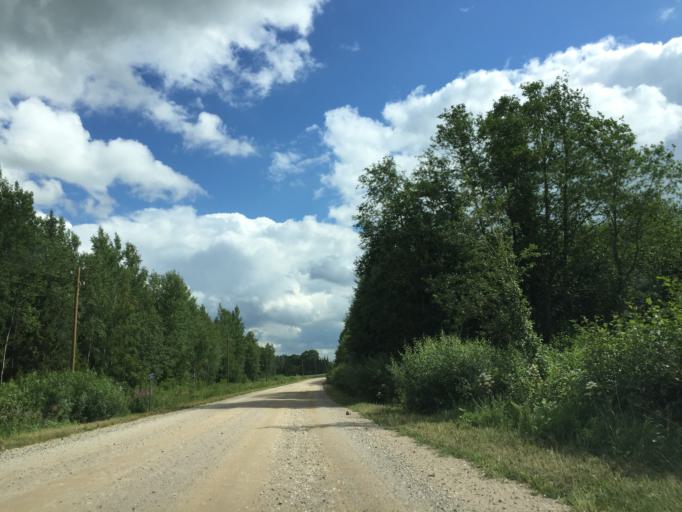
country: LV
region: Malpils
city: Malpils
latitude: 56.8757
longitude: 25.0009
